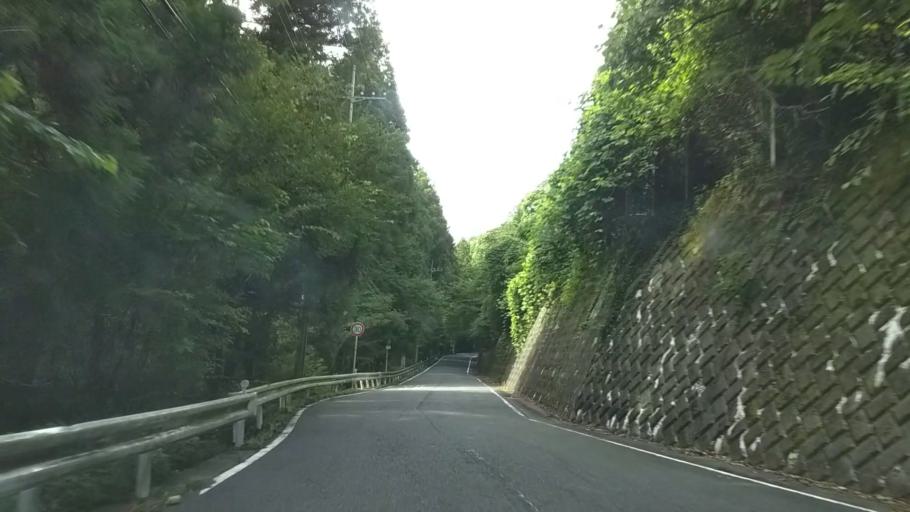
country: JP
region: Yamanashi
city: Uenohara
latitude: 35.5777
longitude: 139.1504
